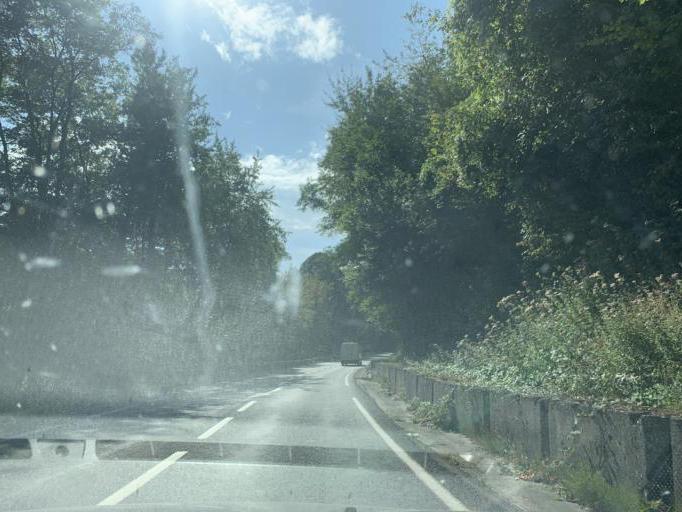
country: FR
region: Rhone-Alpes
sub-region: Departement de l'Ain
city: Divonne-les-Bains
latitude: 46.3570
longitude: 6.1316
